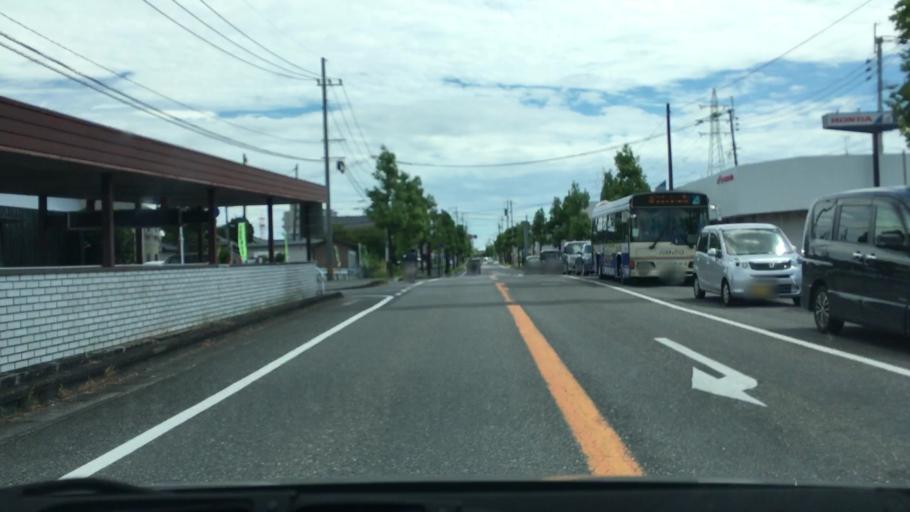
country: JP
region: Saga Prefecture
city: Saga-shi
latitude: 33.2730
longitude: 130.2864
